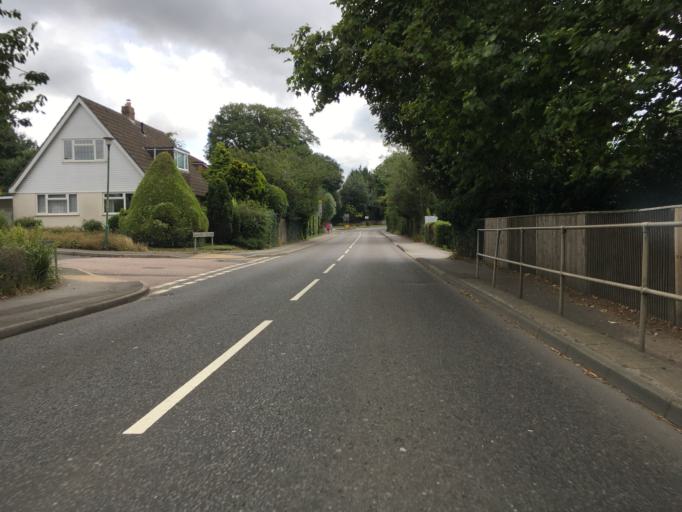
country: GB
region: England
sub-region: Kent
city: Tenterden
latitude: 51.0759
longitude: 0.6941
